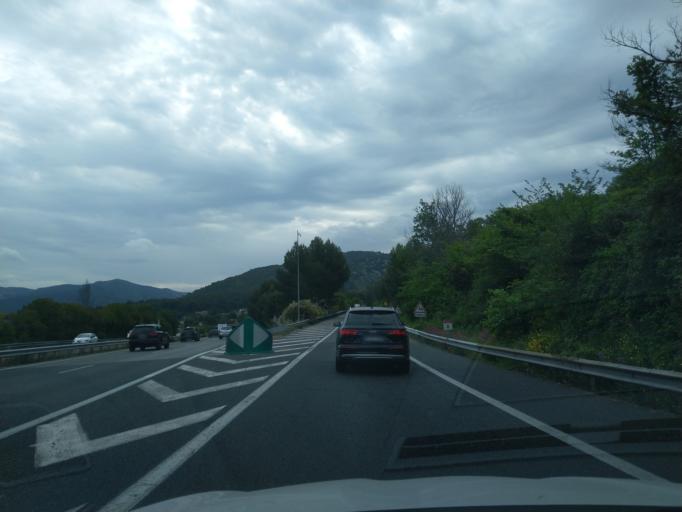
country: FR
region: Provence-Alpes-Cote d'Azur
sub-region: Departement des Bouches-du-Rhone
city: Aubagne
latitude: 43.2836
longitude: 5.5742
